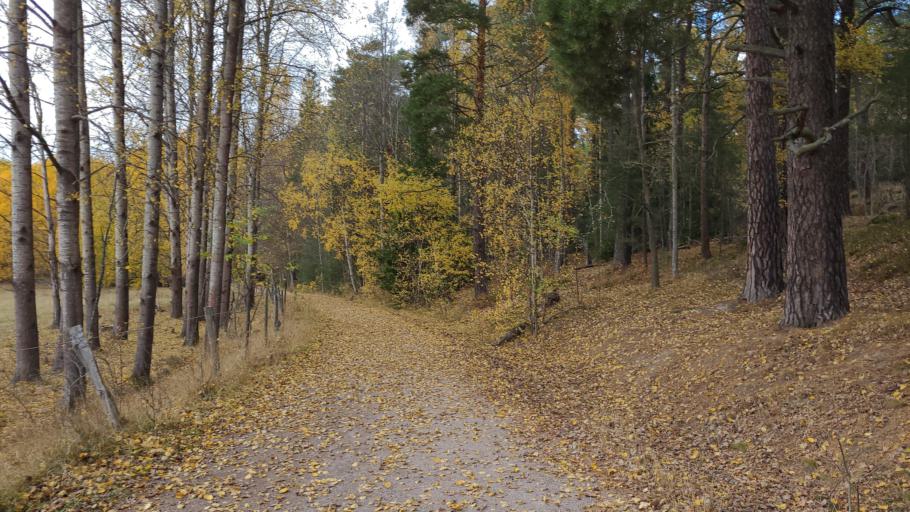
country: SE
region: Stockholm
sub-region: Solna Kommun
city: Rasunda
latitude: 59.3889
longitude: 17.9779
